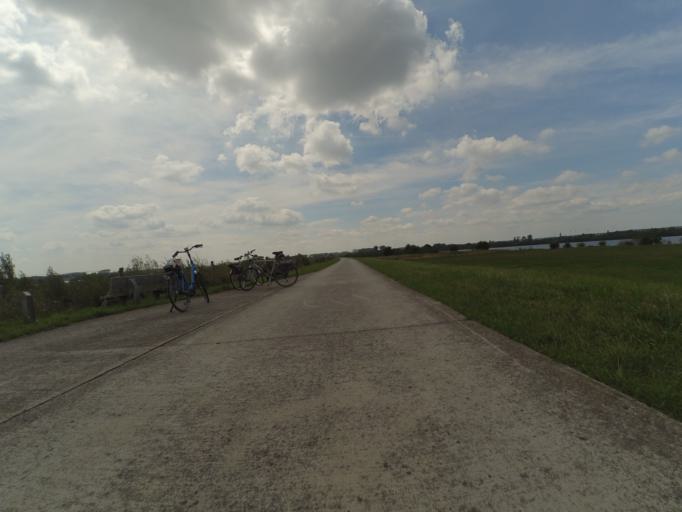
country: BE
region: Flanders
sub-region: Provincie Limburg
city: Maaseik
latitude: 51.0571
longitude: 5.7635
